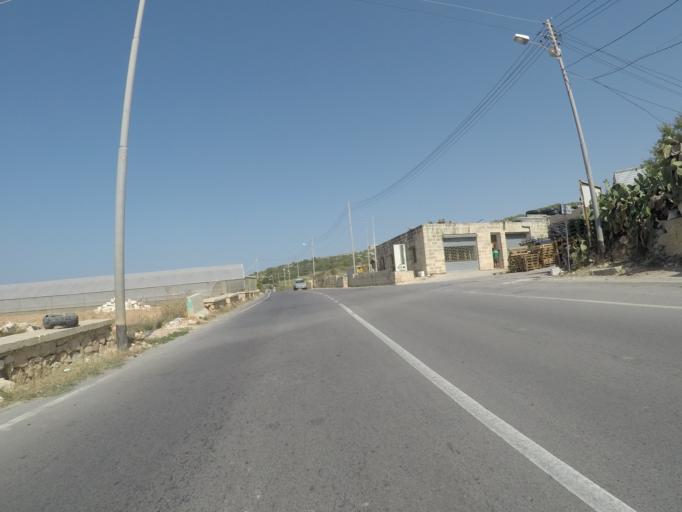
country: MT
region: Il-Mellieha
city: Mellieha
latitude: 35.9413
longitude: 14.3788
